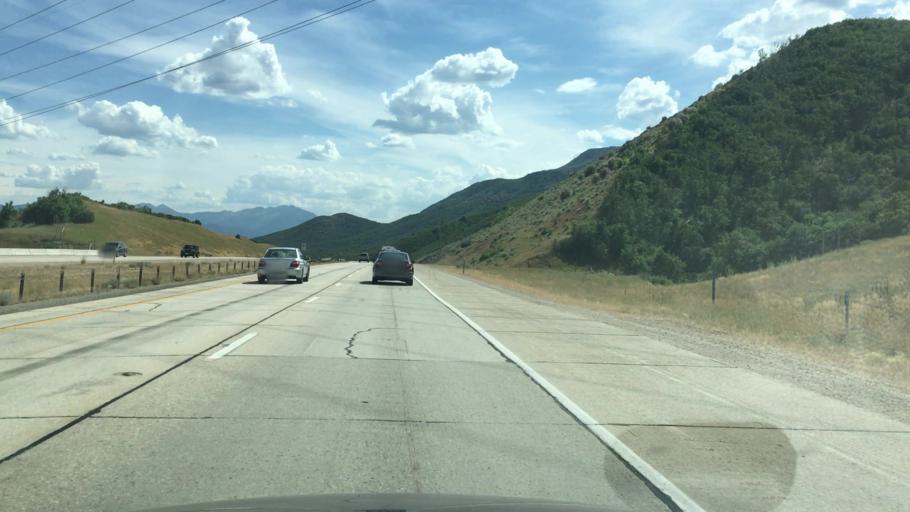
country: US
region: Utah
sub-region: Summit County
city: Park City
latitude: 40.6006
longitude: -111.4319
